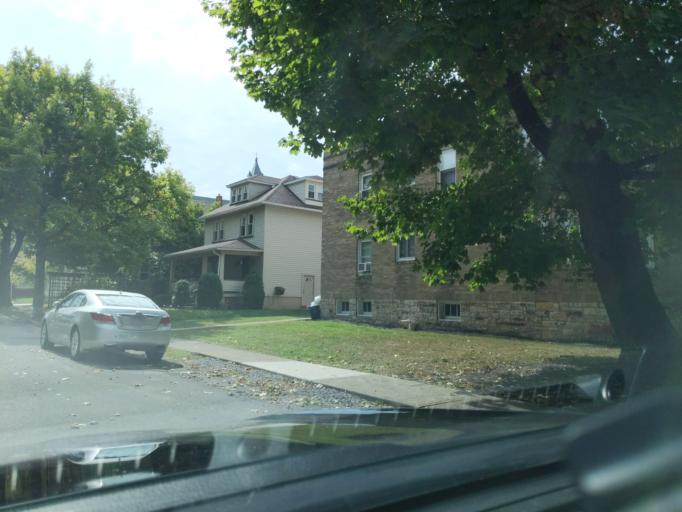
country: US
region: Pennsylvania
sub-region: Blair County
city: Hollidaysburg
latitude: 40.4335
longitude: -78.3901
